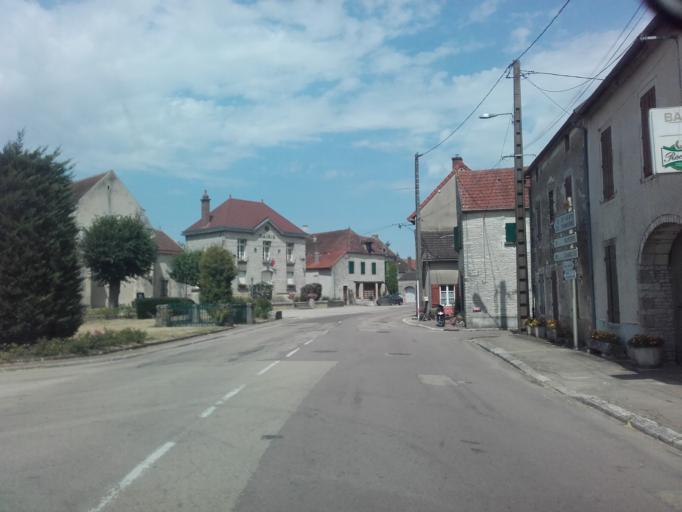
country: FR
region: Bourgogne
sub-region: Departement de l'Yonne
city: Joux-la-Ville
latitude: 47.6720
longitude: 3.8781
